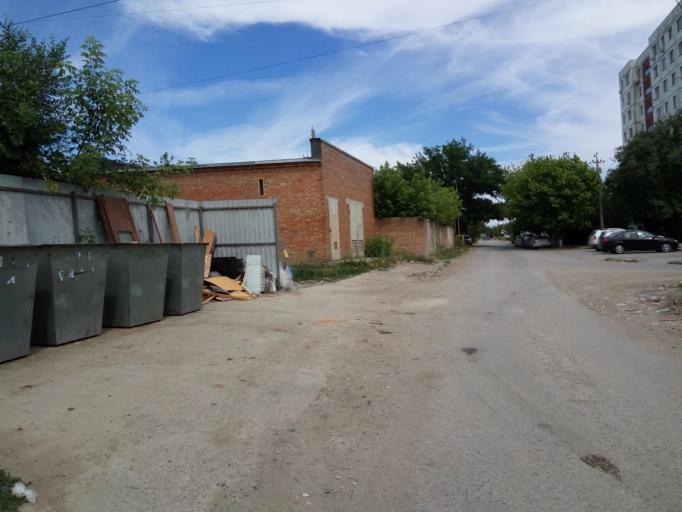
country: RU
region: Rostov
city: Bataysk
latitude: 47.1208
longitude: 39.7324
